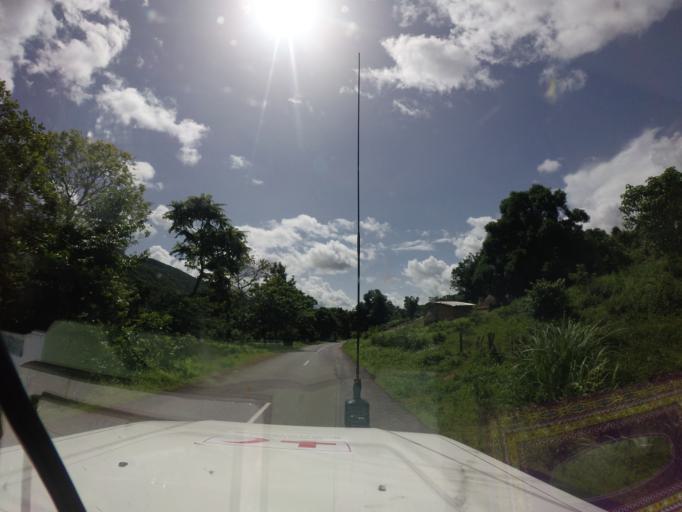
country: GN
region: Mamou
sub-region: Mamou Prefecture
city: Mamou
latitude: 10.2500
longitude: -11.8848
